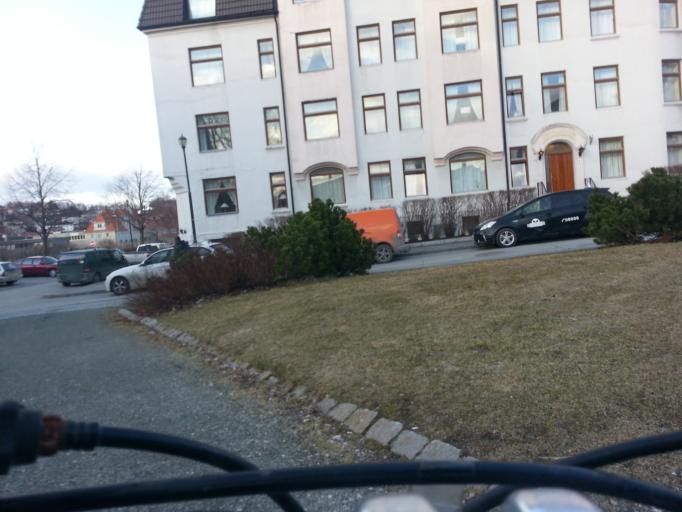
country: NO
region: Sor-Trondelag
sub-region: Trondheim
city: Trondheim
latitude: 63.4401
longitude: 10.4328
